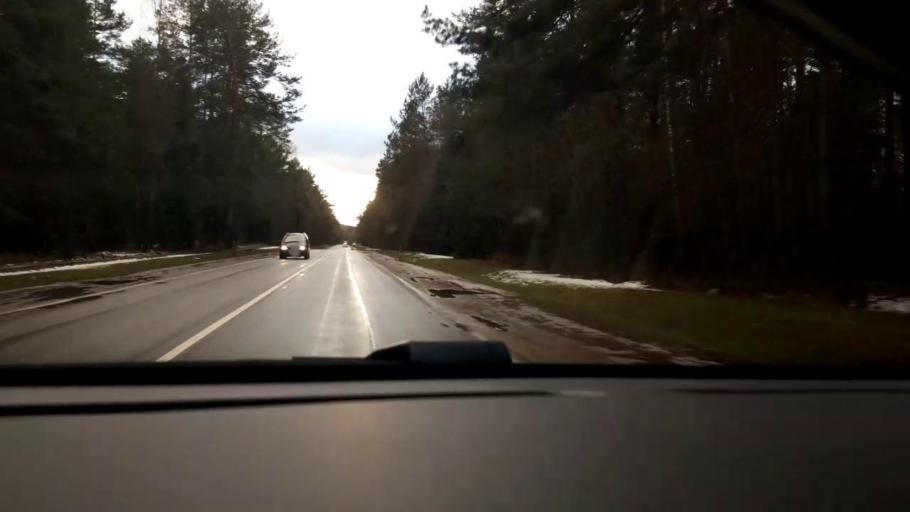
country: LT
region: Vilnius County
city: Rasos
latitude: 54.7690
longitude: 25.3796
